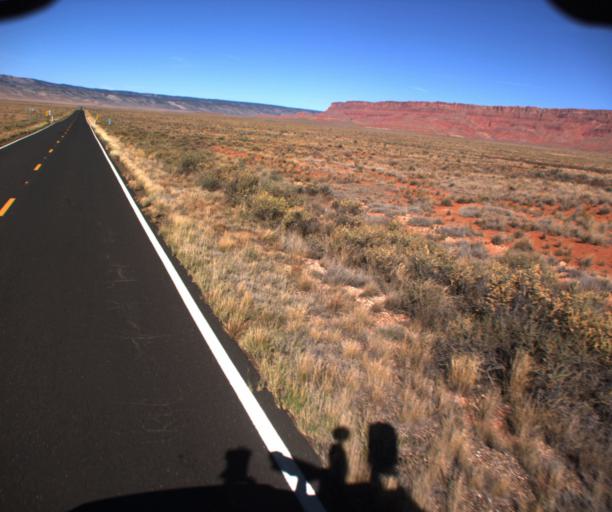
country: US
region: Arizona
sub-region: Coconino County
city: Page
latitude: 36.6972
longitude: -111.9139
